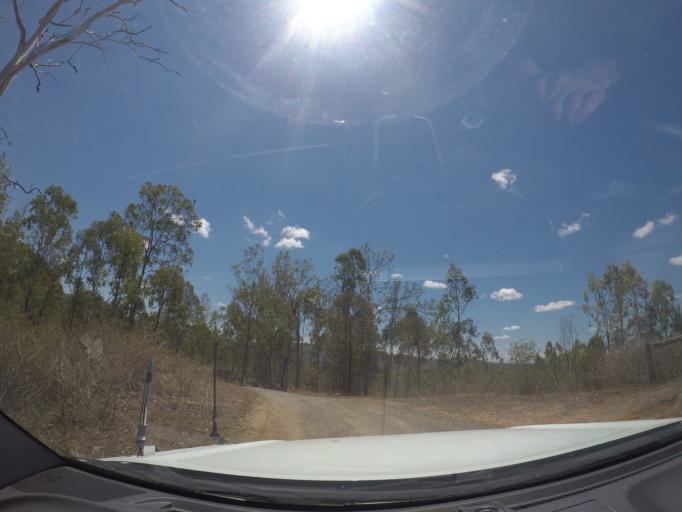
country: AU
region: Queensland
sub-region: Ipswich
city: Deebing Heights
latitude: -27.8286
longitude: 152.8343
